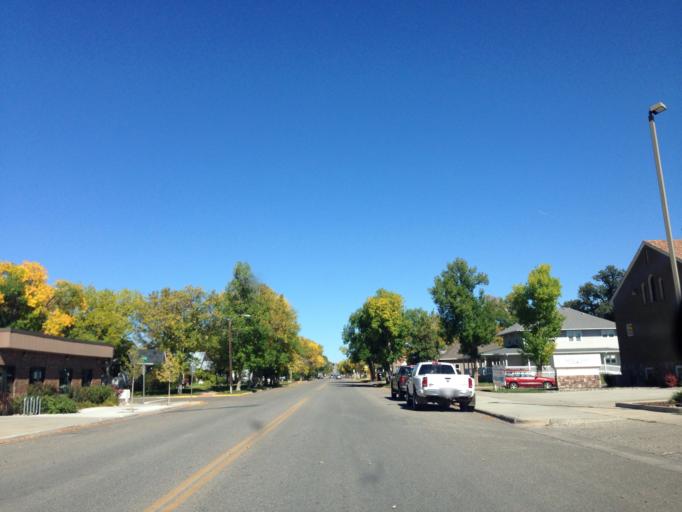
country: US
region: Montana
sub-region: Yellowstone County
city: Laurel
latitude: 45.6708
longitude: -108.7716
